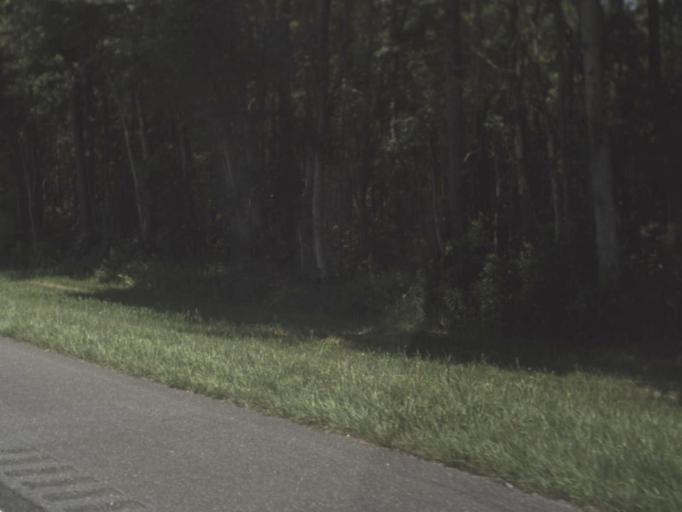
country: US
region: Florida
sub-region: Baker County
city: Macclenny
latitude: 30.2364
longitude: -82.2751
